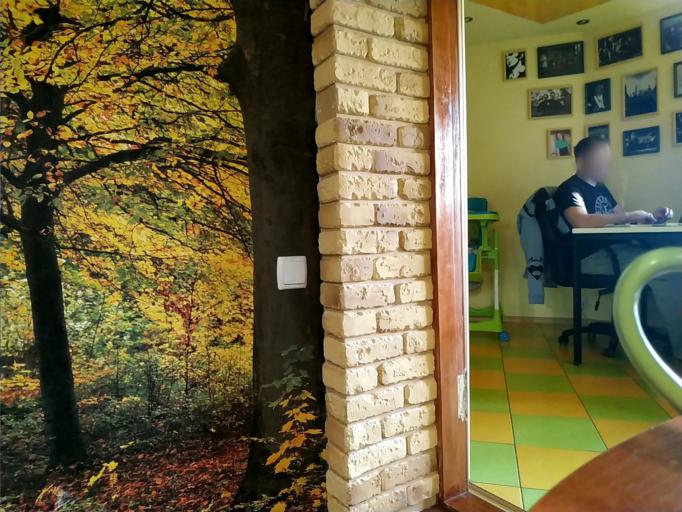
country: RU
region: Jaroslavl
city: Levashevo
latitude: 57.8155
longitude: 40.6521
